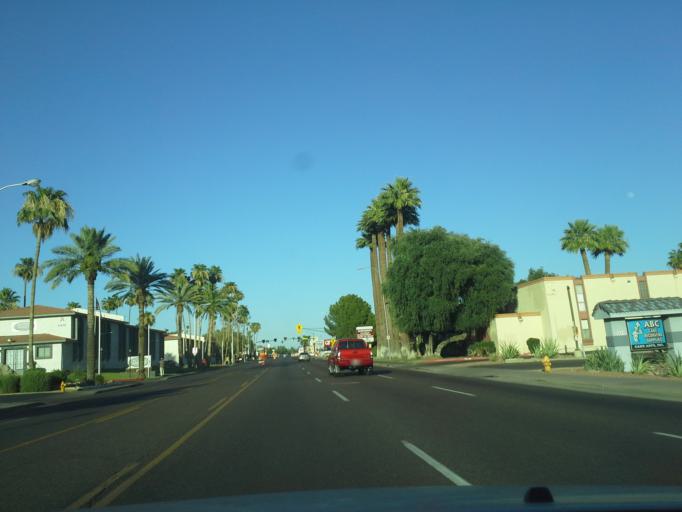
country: US
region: Arizona
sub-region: Maricopa County
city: Phoenix
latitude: 33.4951
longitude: -112.0200
